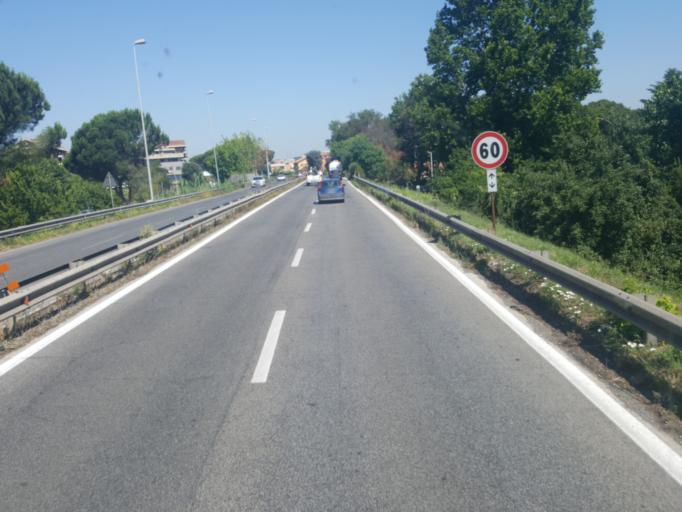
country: IT
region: Latium
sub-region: Citta metropolitana di Roma Capitale
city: Ciampino
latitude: 41.8296
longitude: 12.6211
